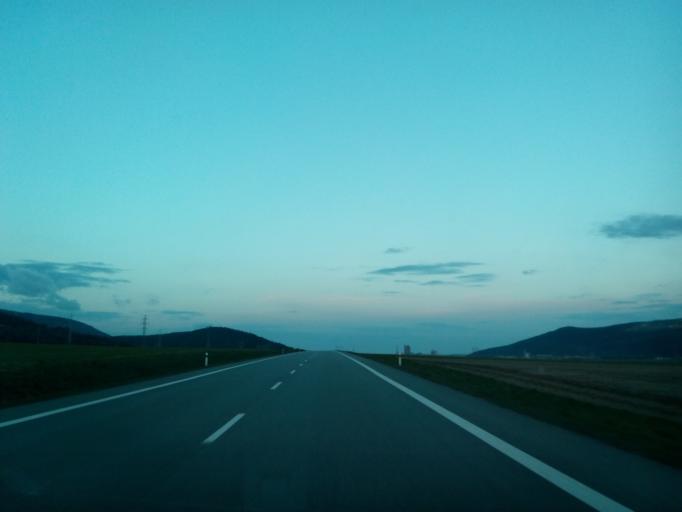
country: SK
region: Kosicky
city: Medzev
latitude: 48.6005
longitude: 20.7753
